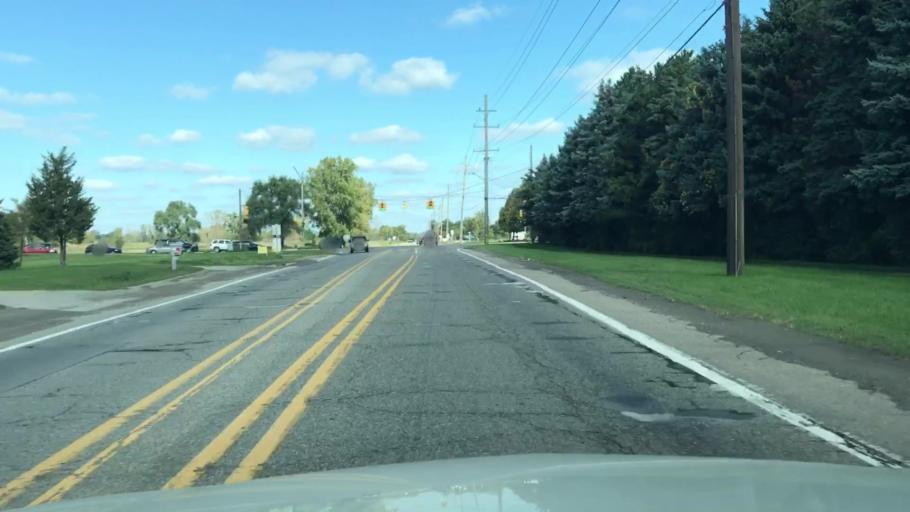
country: US
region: Michigan
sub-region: Oakland County
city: Rochester
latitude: 42.6522
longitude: -83.0927
